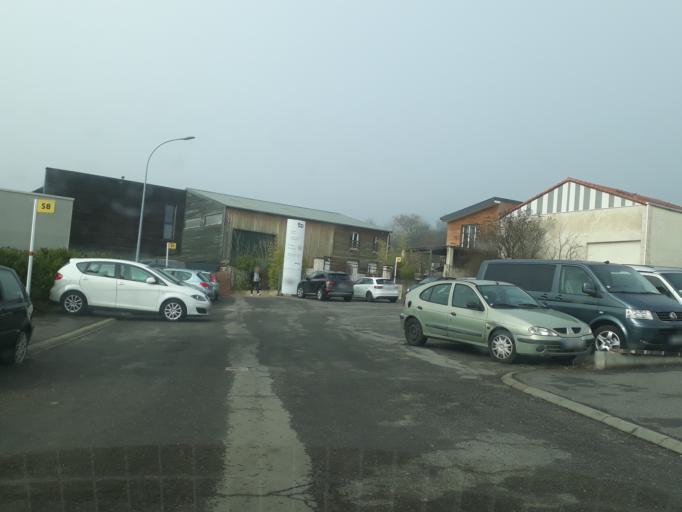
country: FR
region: Lorraine
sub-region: Departement de Meurthe-et-Moselle
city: Bouxieres-aux-Dames
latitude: 48.7465
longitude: 6.1806
